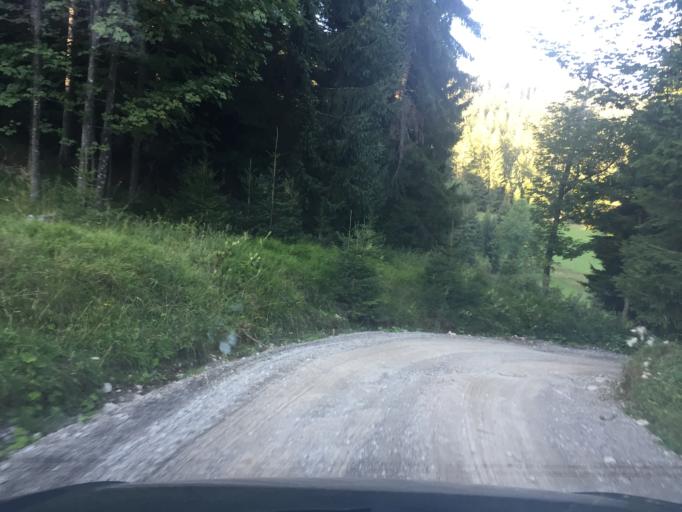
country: SI
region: Ravne na Koroskem
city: Kotlje
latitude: 46.4776
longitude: 14.9803
